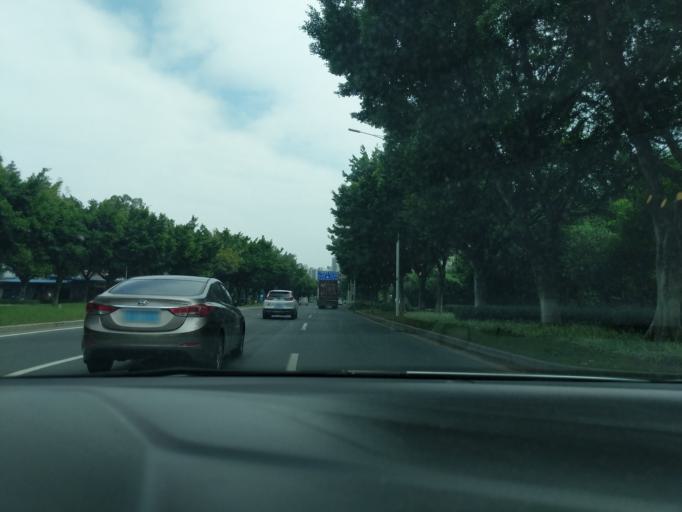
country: CN
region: Guangdong
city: Nansha
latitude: 22.7536
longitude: 113.5758
